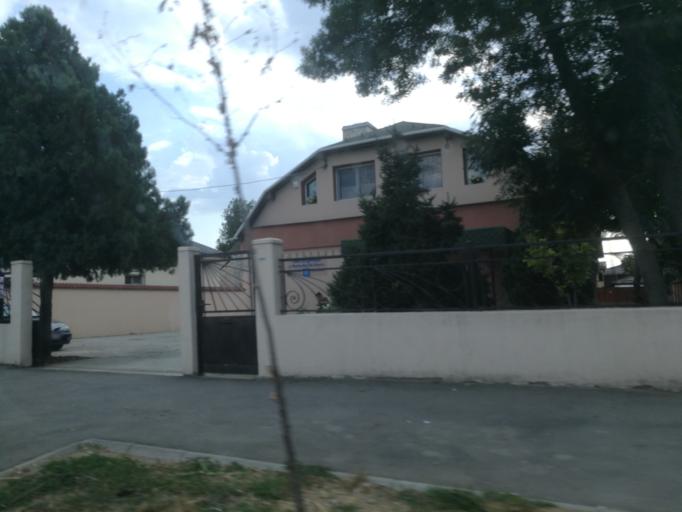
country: RO
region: Ilfov
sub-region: Comuna Mogosoaia
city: Mogosoaia
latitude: 44.5001
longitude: 26.0272
